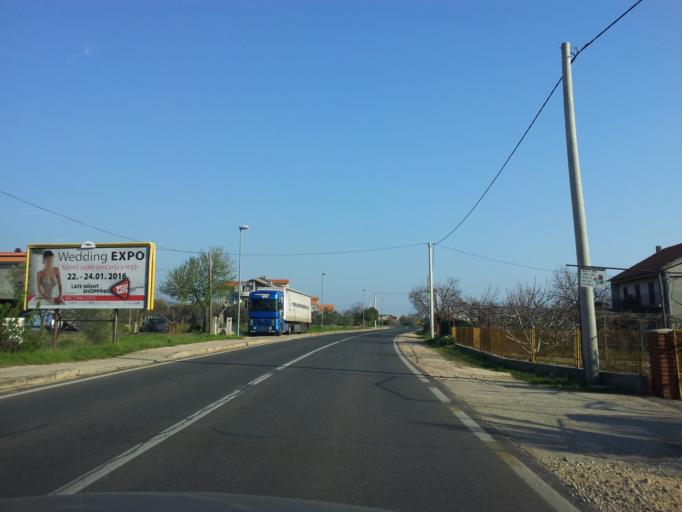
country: HR
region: Zadarska
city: Sukosan
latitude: 44.0419
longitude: 15.3202
